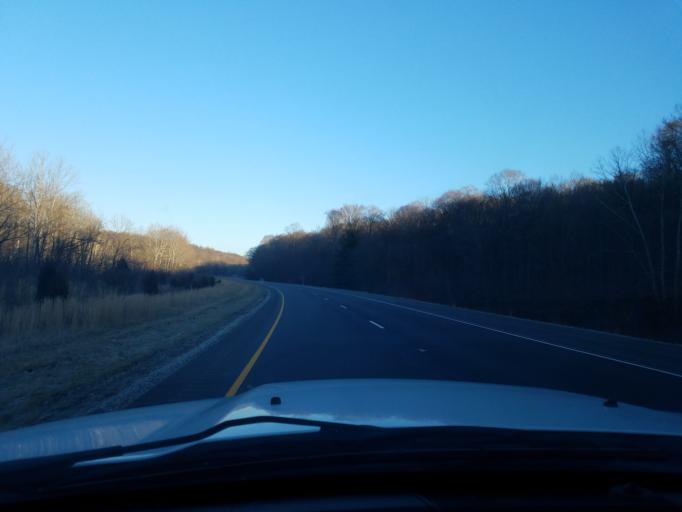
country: US
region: Indiana
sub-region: Crawford County
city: English
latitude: 38.2376
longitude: -86.4022
